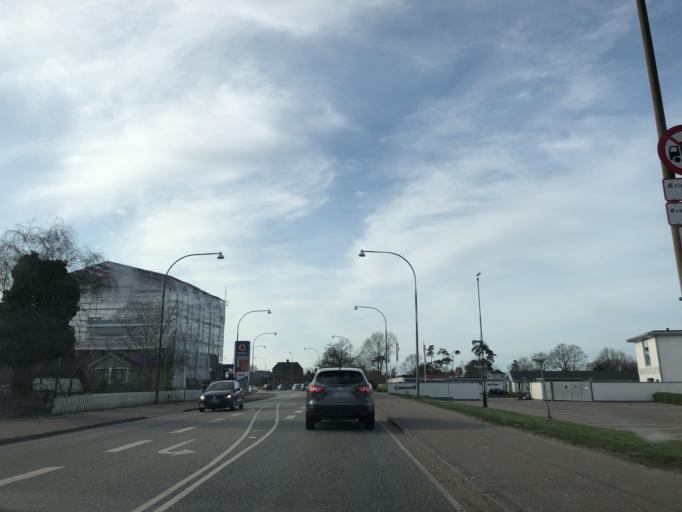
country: DK
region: Zealand
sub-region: Koge Kommune
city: Koge
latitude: 55.4467
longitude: 12.1918
